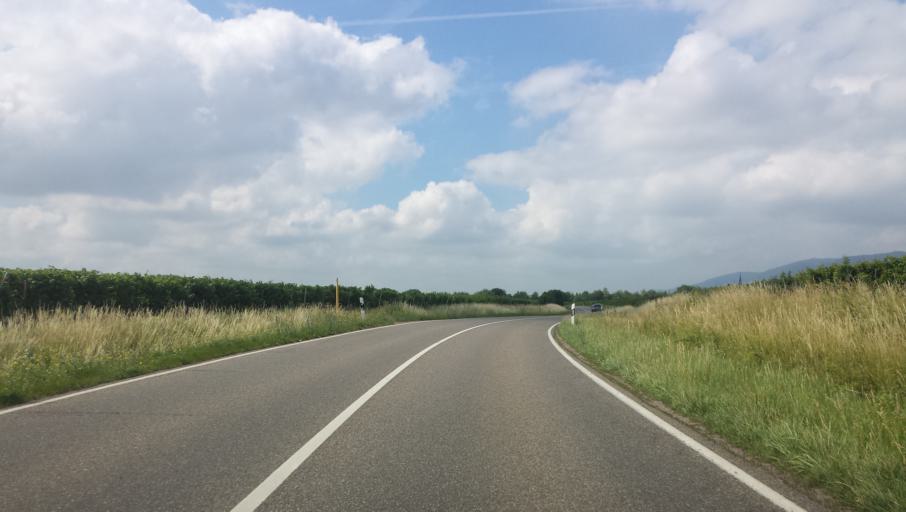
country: DE
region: Rheinland-Pfalz
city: Maikammer
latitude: 49.3170
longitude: 8.1476
